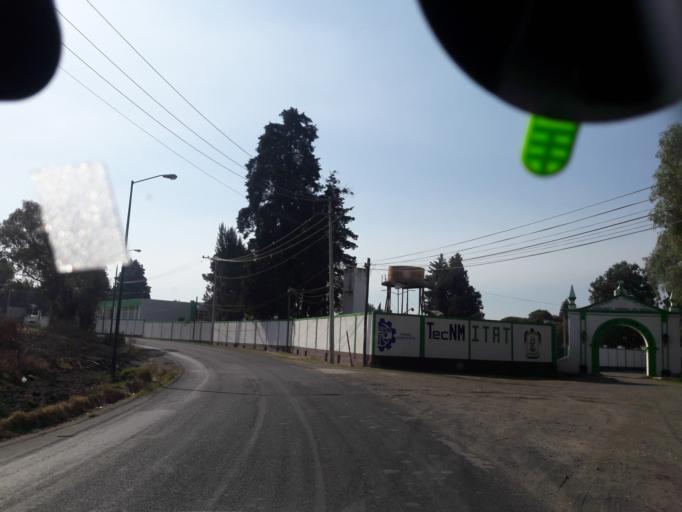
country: MX
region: Tlaxcala
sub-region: Ixtacuixtla de Mariano Matamoros
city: Villa Mariano Matamoros
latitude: 19.3105
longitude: -98.3854
